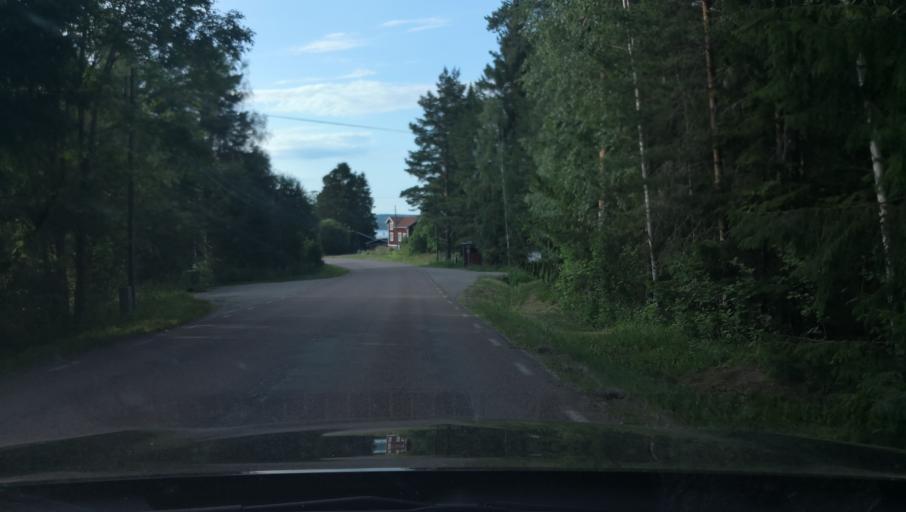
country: SE
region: Dalarna
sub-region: Ludvika Kommun
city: Ludvika
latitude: 60.0701
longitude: 15.2541
